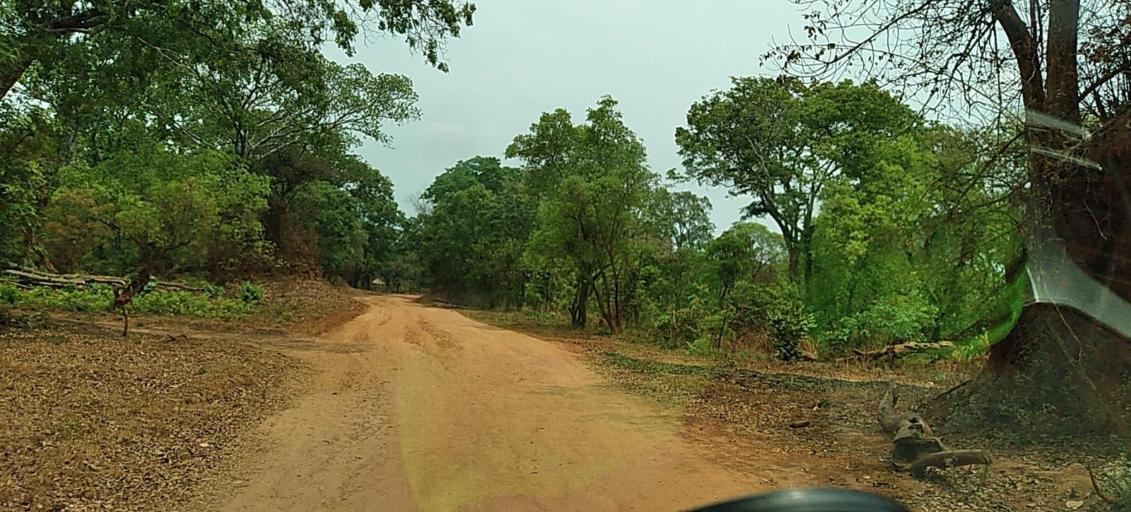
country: ZM
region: North-Western
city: Solwezi
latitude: -12.8050
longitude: 26.5378
